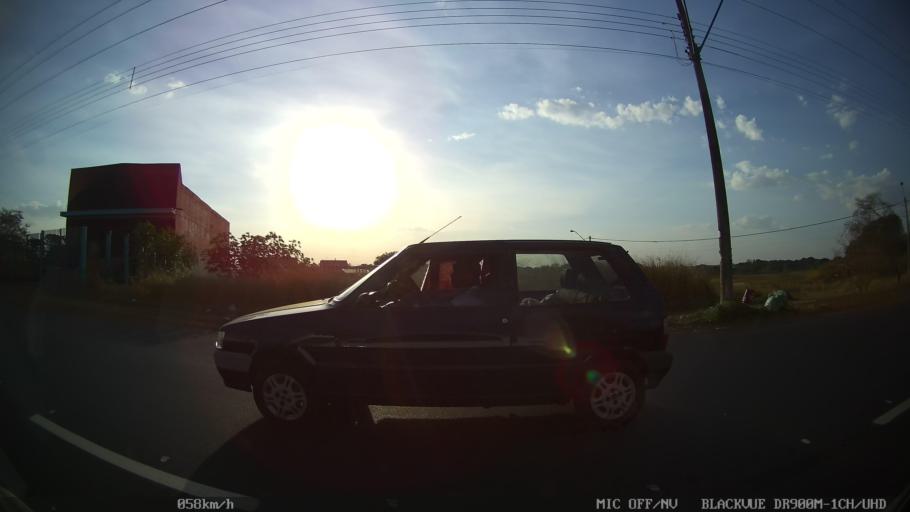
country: BR
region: Sao Paulo
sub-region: Ribeirao Preto
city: Ribeirao Preto
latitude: -21.1308
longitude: -47.7937
